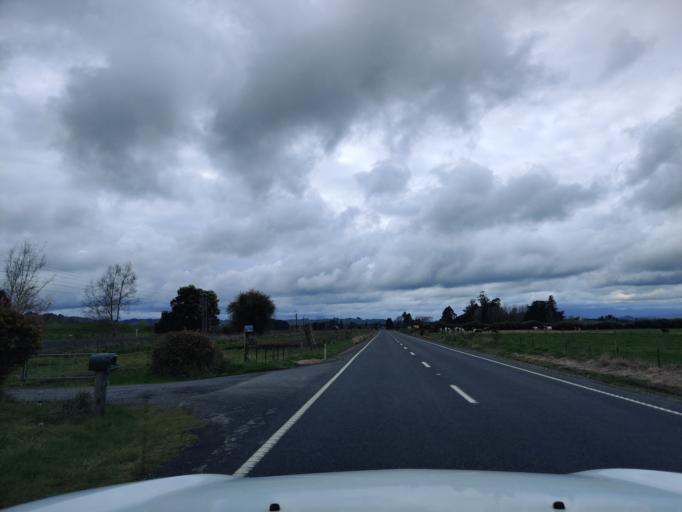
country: NZ
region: Waikato
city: Turangi
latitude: -39.0220
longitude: 175.3797
